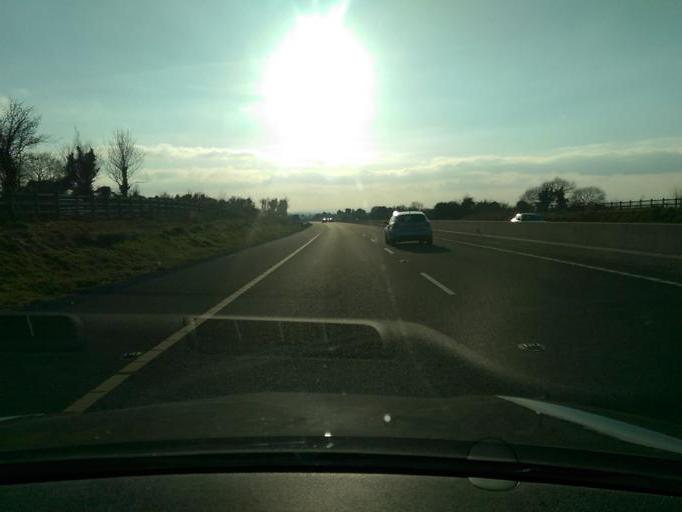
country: IE
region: Munster
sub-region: North Tipperary
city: Roscrea
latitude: 52.9087
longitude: -7.8775
